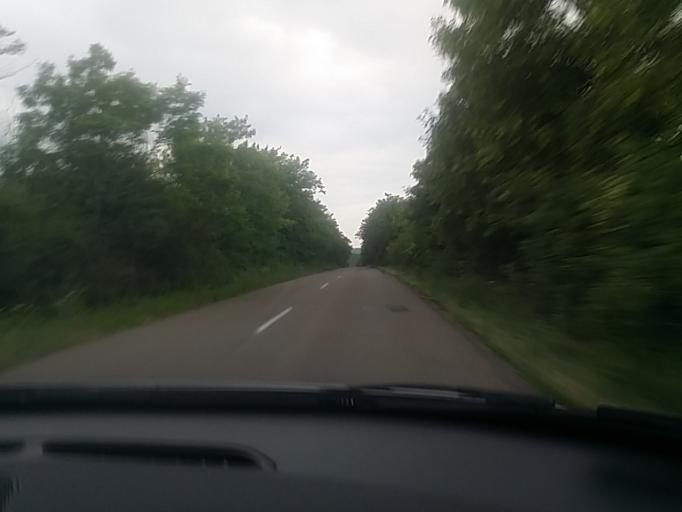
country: HU
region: Nograd
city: Paszto
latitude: 47.9111
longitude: 19.6550
